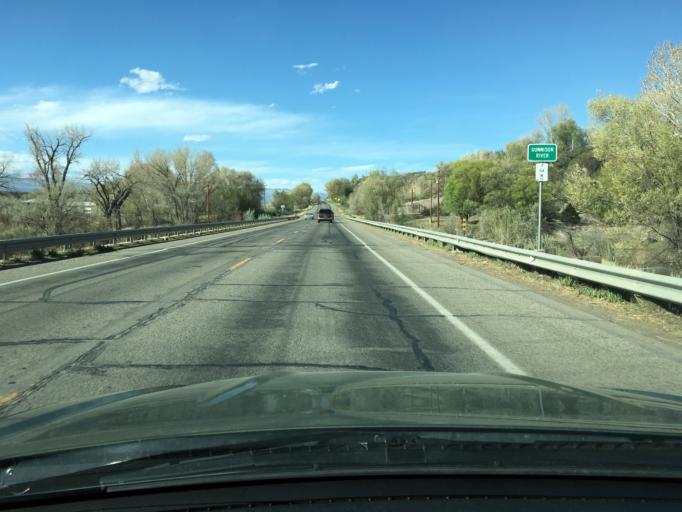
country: US
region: Colorado
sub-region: Delta County
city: Orchard City
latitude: 38.7721
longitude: -108.0028
